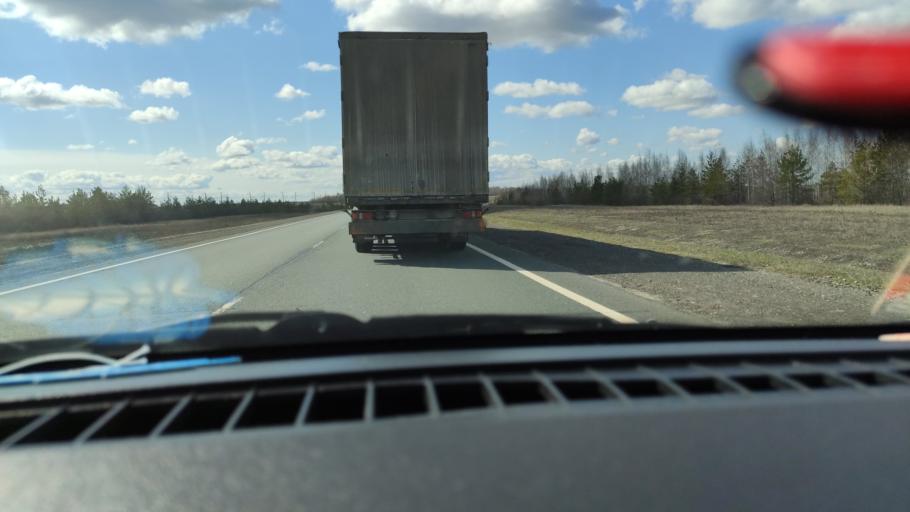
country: RU
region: Samara
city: Syzran'
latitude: 52.8753
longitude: 48.2892
